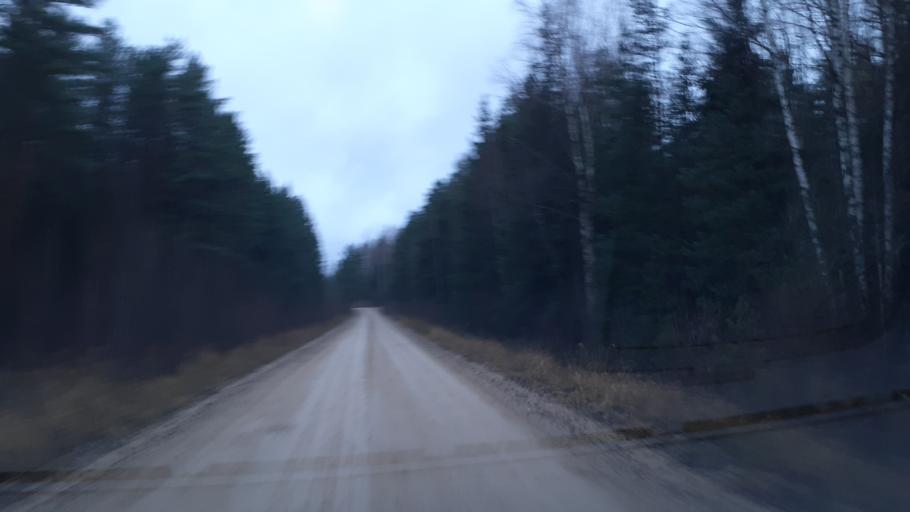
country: LV
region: Kuldigas Rajons
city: Kuldiga
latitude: 57.0512
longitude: 22.1248
